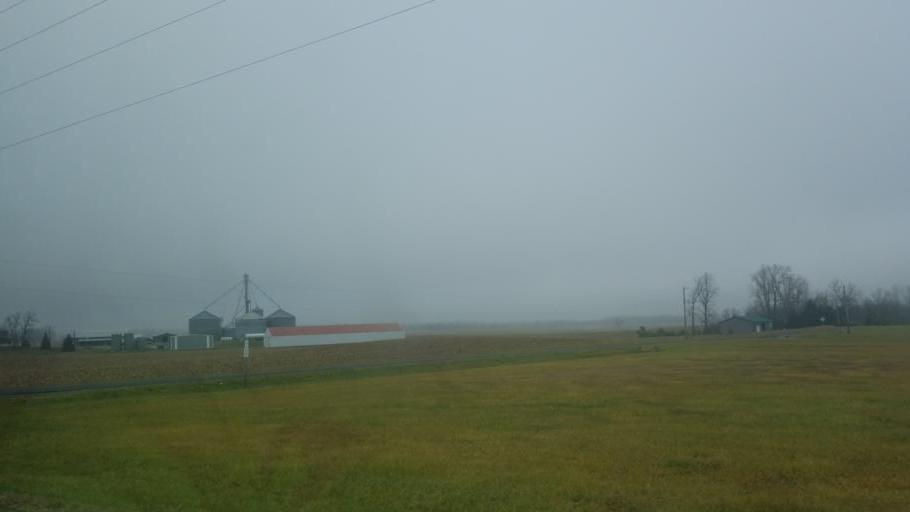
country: US
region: Ohio
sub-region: Champaign County
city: North Lewisburg
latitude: 40.2547
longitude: -83.5809
